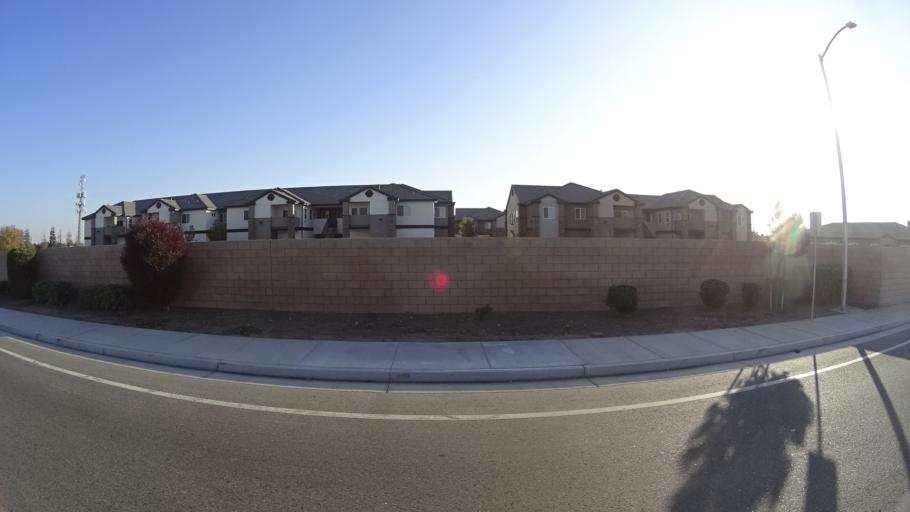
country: US
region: California
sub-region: Kern County
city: Greenfield
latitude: 35.2958
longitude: -119.0600
